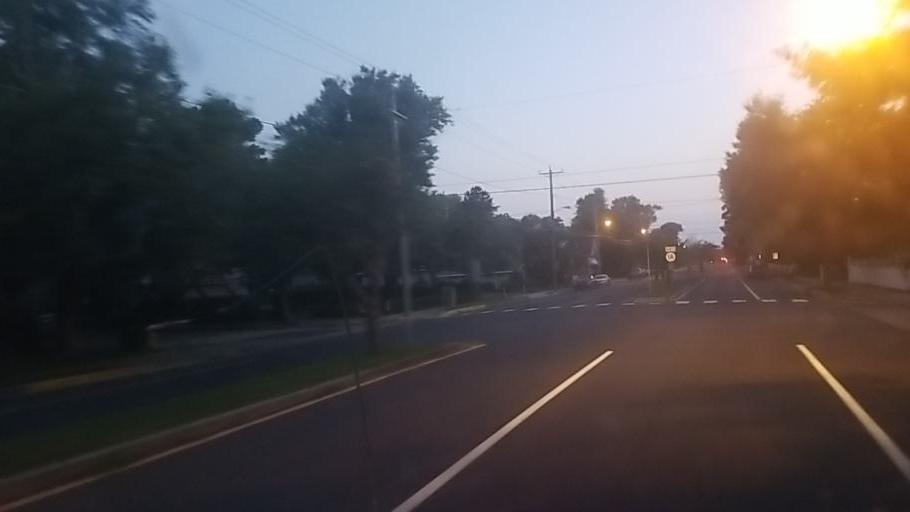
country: US
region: Delaware
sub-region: Sussex County
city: Rehoboth Beach
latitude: 38.7091
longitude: -75.0810
